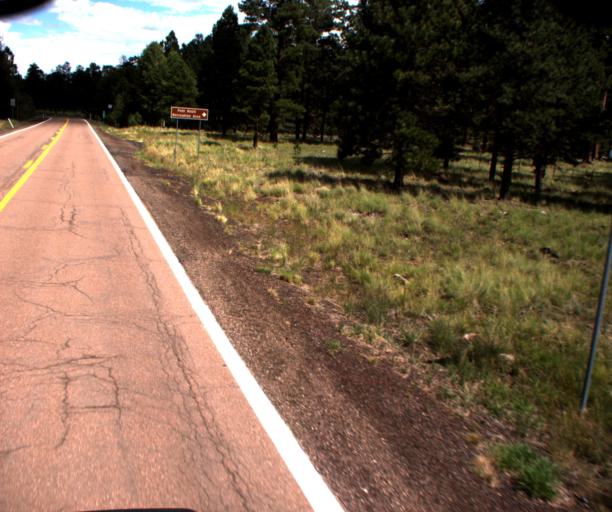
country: US
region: Arizona
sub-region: Apache County
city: Eagar
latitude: 34.0570
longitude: -109.5023
